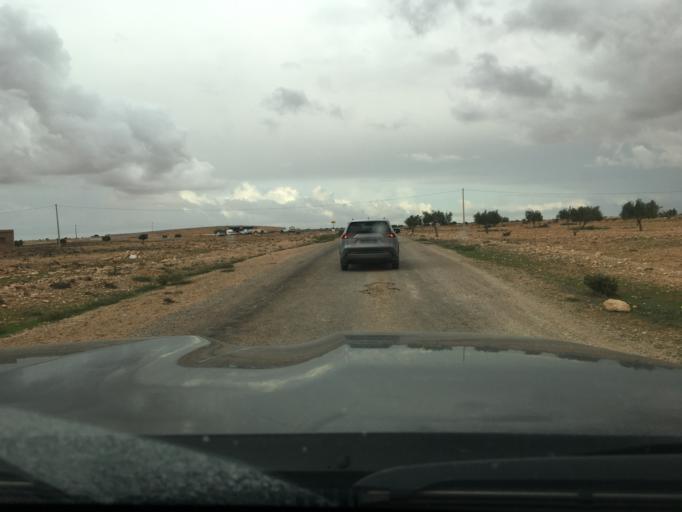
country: TN
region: Madanin
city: Medenine
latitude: 33.2947
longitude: 10.6090
